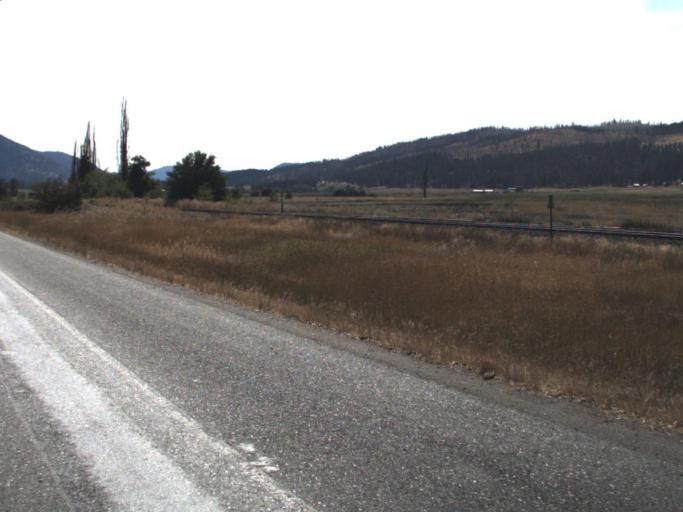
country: US
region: Washington
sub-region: Stevens County
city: Colville
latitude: 48.4520
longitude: -117.8756
